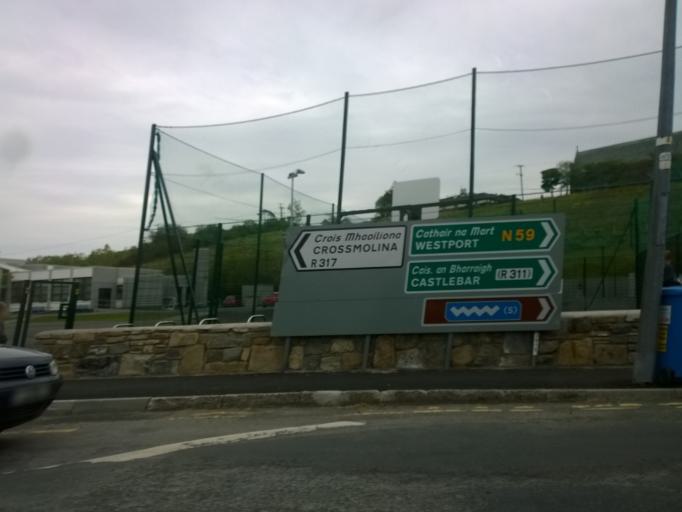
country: IE
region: Connaught
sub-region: Maigh Eo
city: Westport
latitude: 53.8869
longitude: -9.5446
